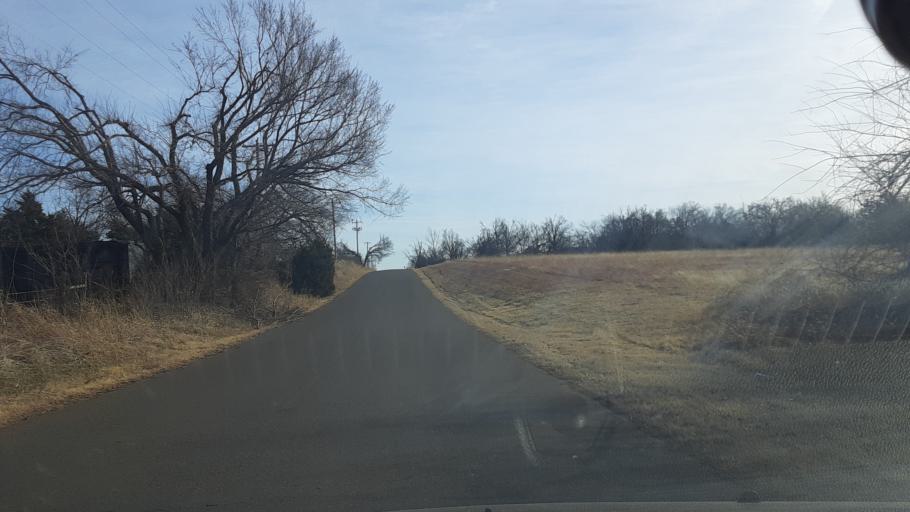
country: US
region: Oklahoma
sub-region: Logan County
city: Guthrie
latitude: 35.8924
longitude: -97.4137
